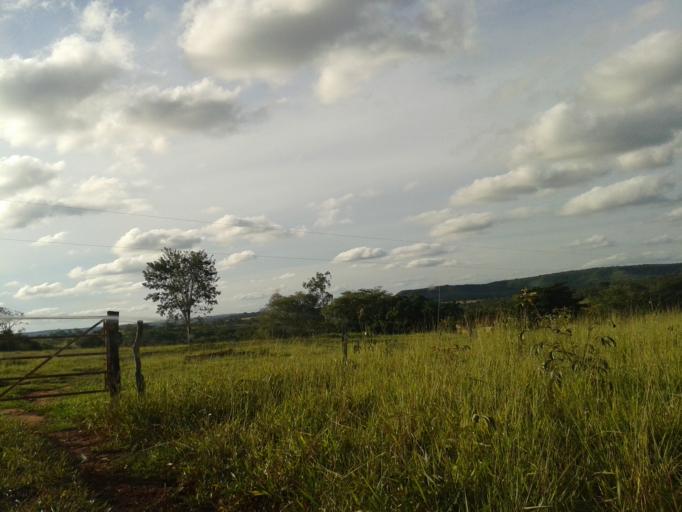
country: BR
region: Minas Gerais
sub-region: Campina Verde
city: Campina Verde
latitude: -19.4110
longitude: -49.7452
